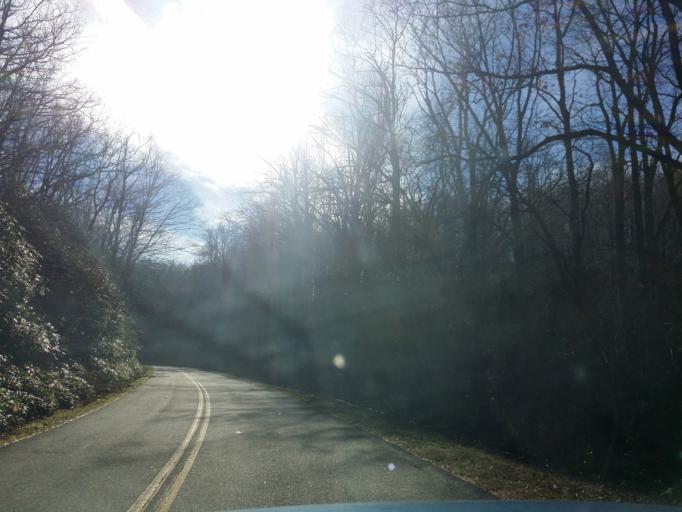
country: US
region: North Carolina
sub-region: McDowell County
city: West Marion
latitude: 35.7571
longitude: -82.1831
